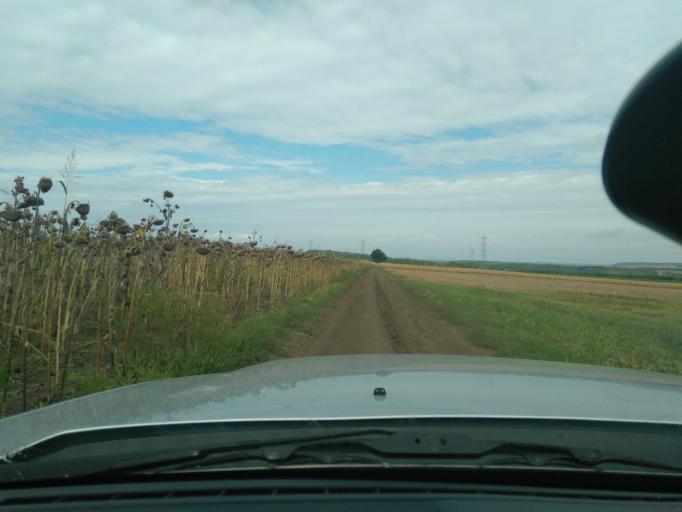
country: HU
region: Fejer
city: Val
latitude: 47.3676
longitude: 18.7012
